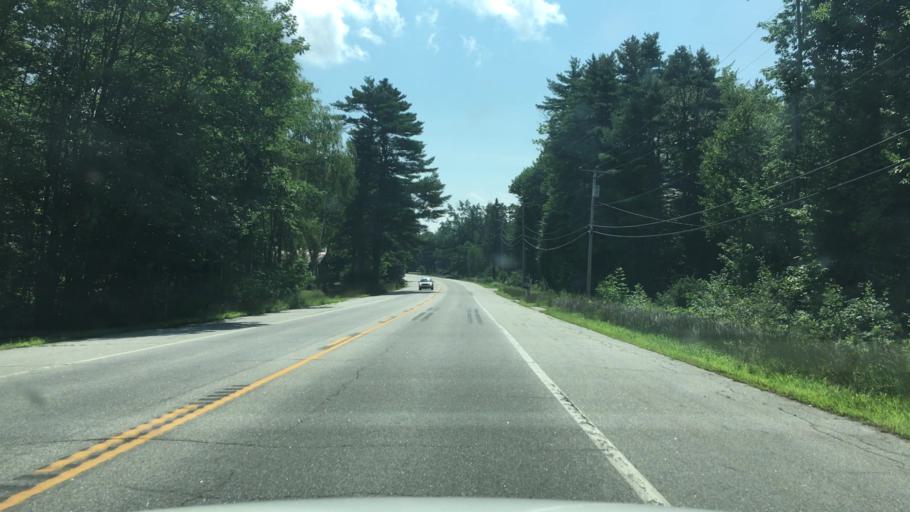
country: US
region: Maine
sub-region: Cumberland County
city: Raymond
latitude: 43.9309
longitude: -70.5381
